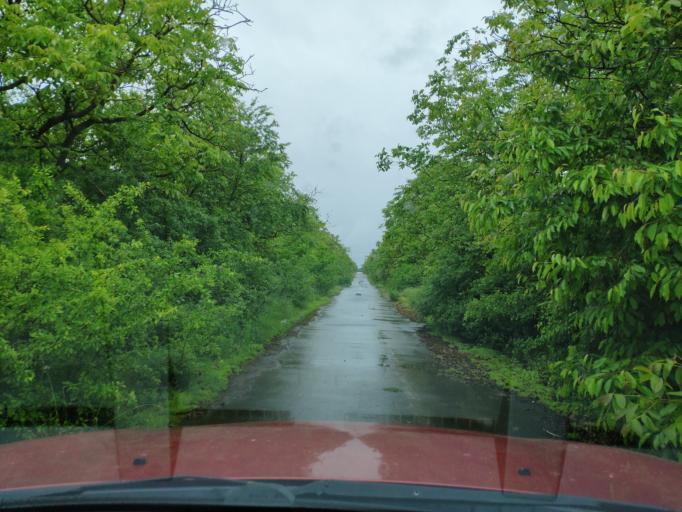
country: SK
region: Kosicky
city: Cierna nad Tisou
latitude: 48.4199
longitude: 22.0563
